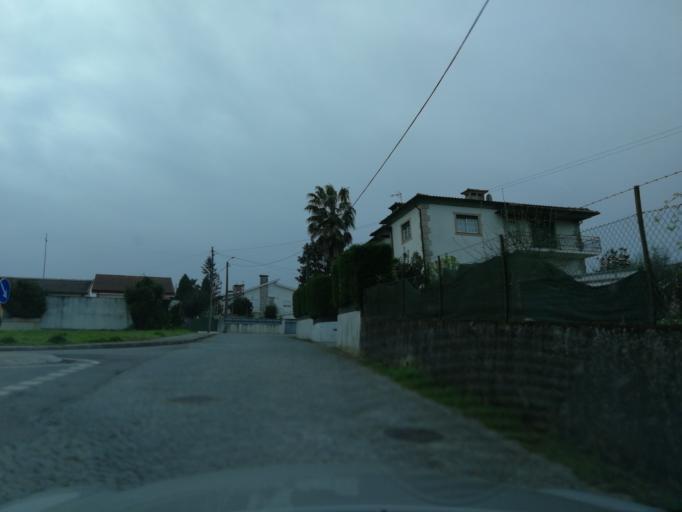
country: PT
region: Braga
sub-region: Braga
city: Braga
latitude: 41.5698
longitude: -8.4394
